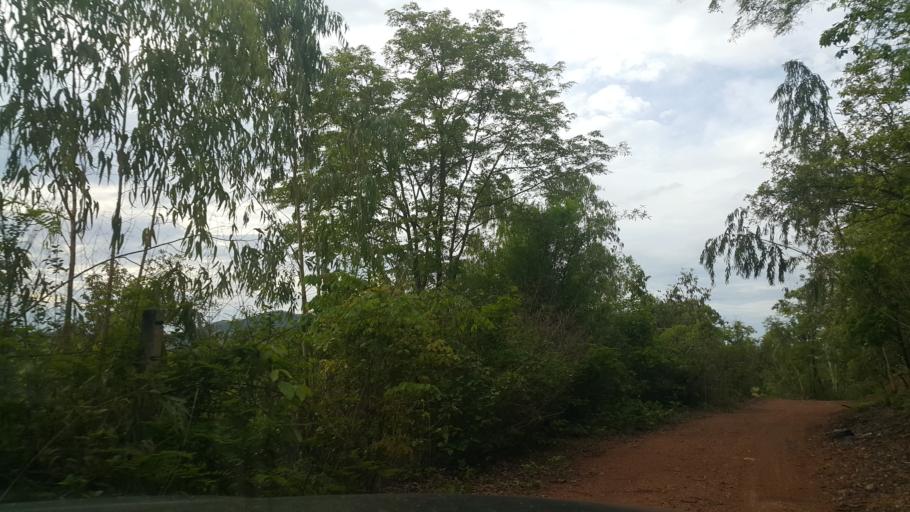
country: TH
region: Chiang Mai
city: Mae On
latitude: 18.7211
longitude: 99.2181
